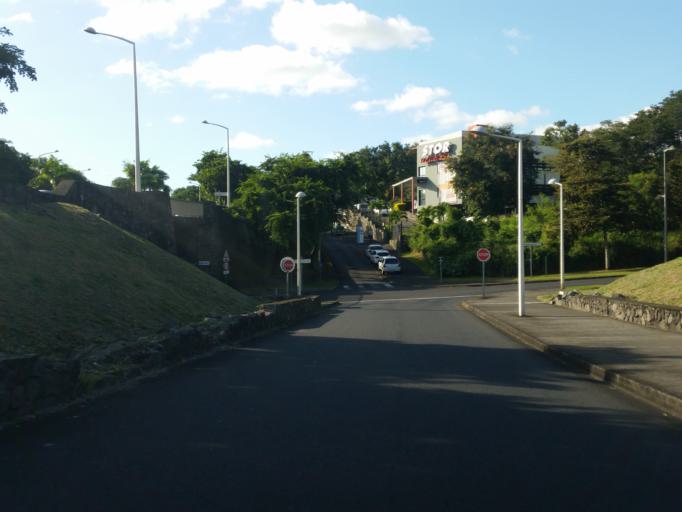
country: RE
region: Reunion
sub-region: Reunion
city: Sainte-Marie
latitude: -20.9023
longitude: 55.4986
